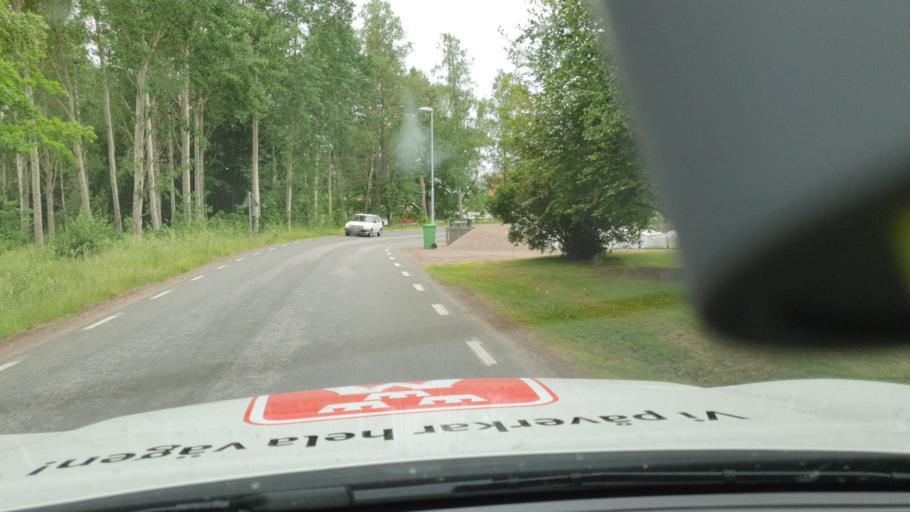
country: SE
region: Vaestra Goetaland
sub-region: Tidaholms Kommun
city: Olofstorp
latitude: 58.3440
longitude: 14.0472
